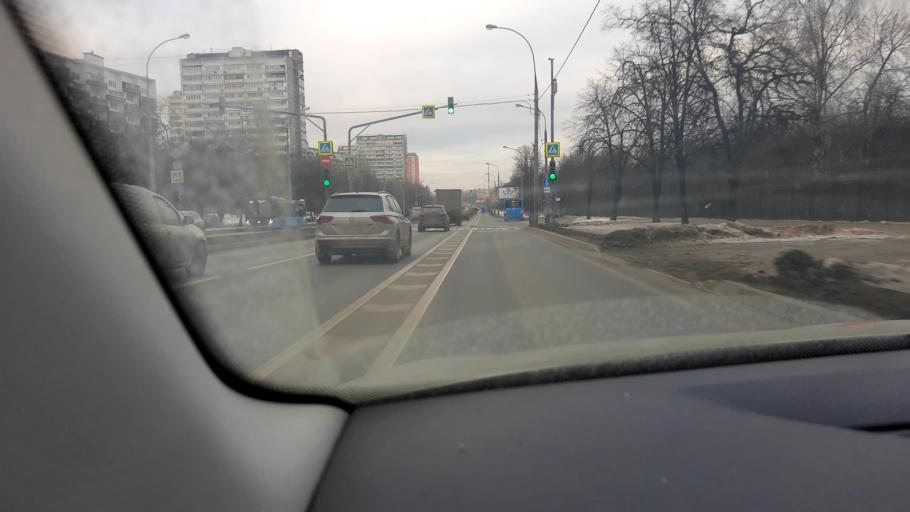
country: RU
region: Moscow
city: Biryulevo
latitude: 55.5966
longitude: 37.6728
